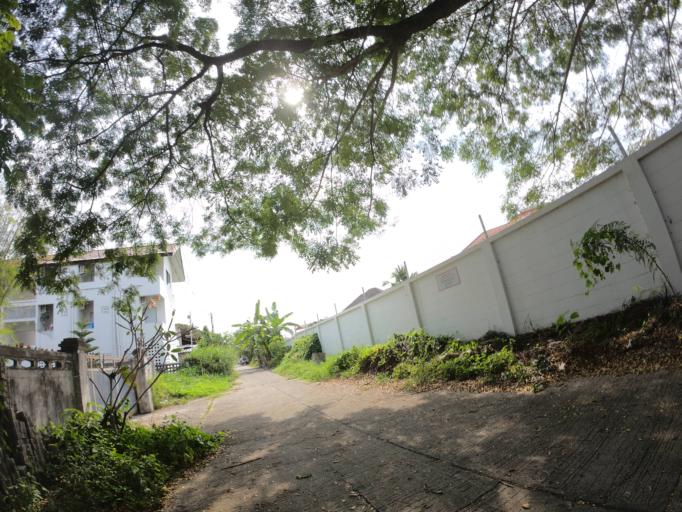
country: TH
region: Chiang Mai
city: Chiang Mai
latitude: 18.7577
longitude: 98.9667
